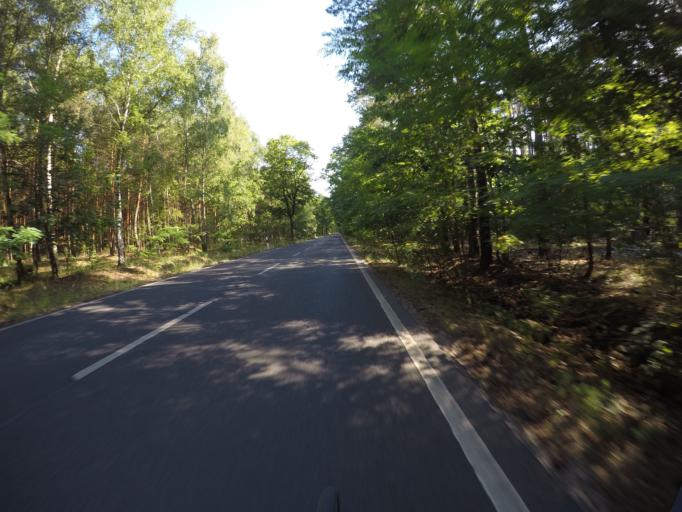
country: DE
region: Berlin
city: Schmockwitz
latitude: 52.3552
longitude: 13.6493
